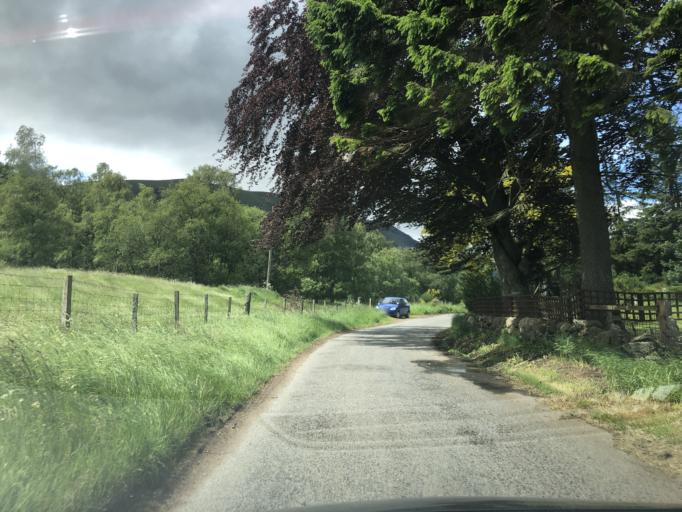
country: GB
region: Scotland
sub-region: Angus
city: Kirriemuir
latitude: 56.8380
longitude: -3.0982
